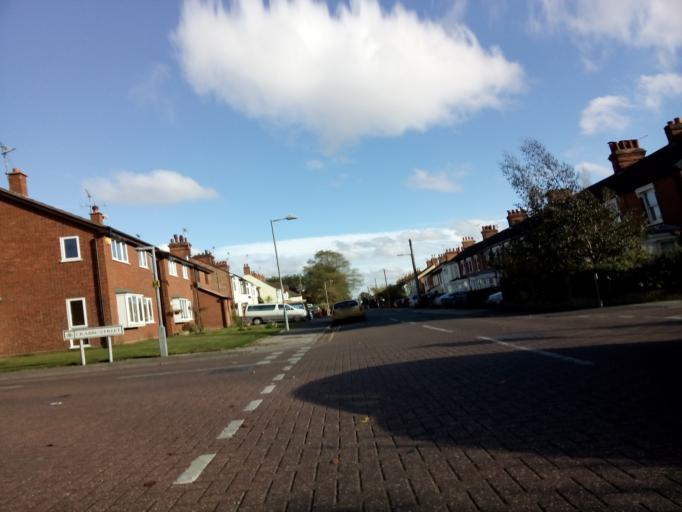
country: GB
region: England
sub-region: Suffolk
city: Ipswich
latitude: 52.0561
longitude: 1.1839
